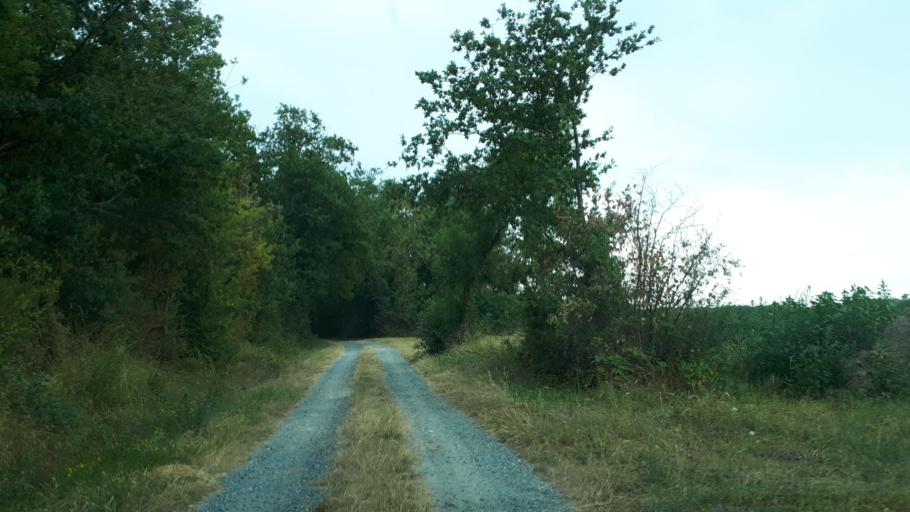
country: FR
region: Centre
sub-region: Departement du Loir-et-Cher
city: Saint-Romain-sur-Cher
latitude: 47.3542
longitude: 1.3935
